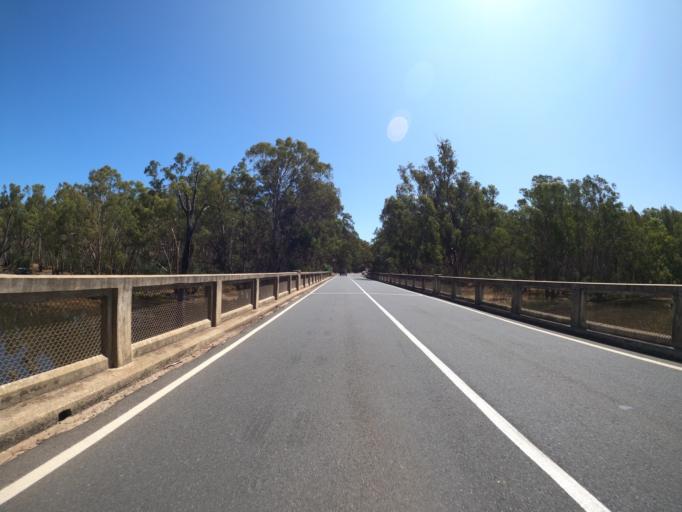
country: AU
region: New South Wales
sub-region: Corowa Shire
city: Corowa
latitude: -36.0688
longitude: 146.1994
